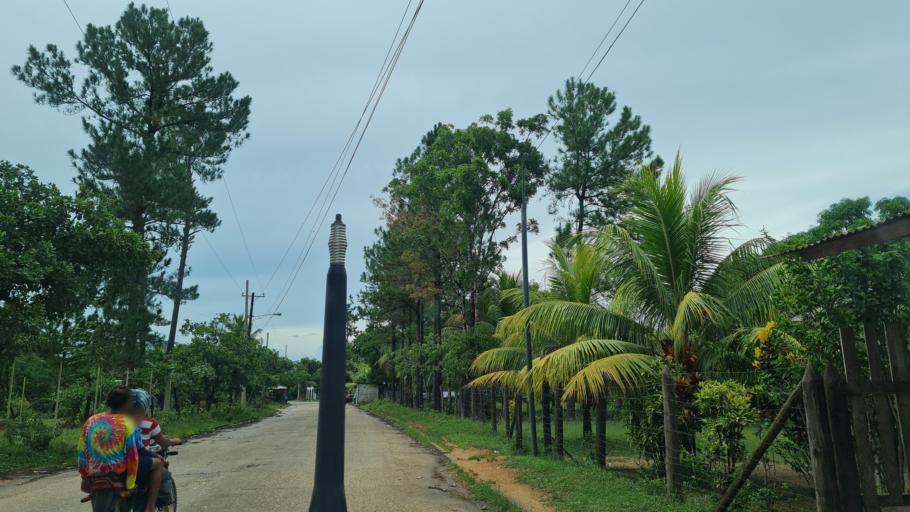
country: NI
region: Atlantico Norte (RAAN)
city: Waspam
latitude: 14.7302
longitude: -83.9692
